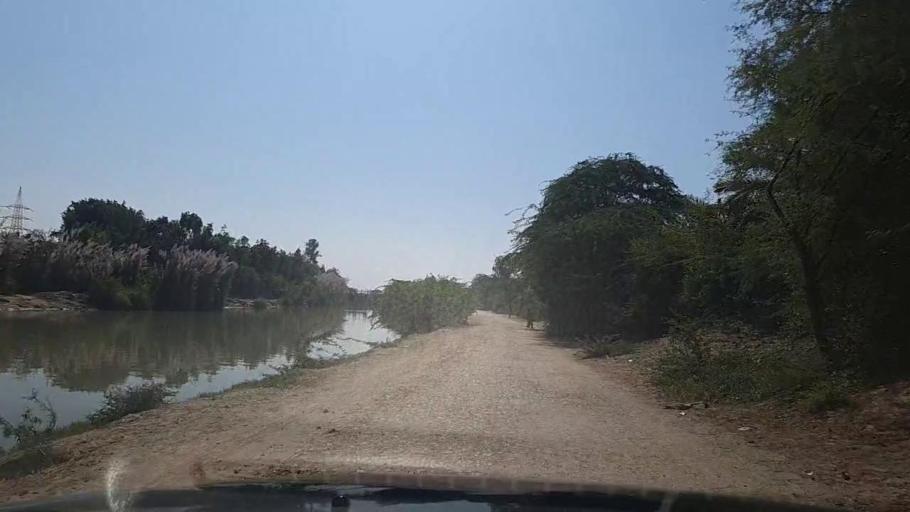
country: PK
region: Sindh
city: Thatta
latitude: 24.5979
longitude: 67.8199
